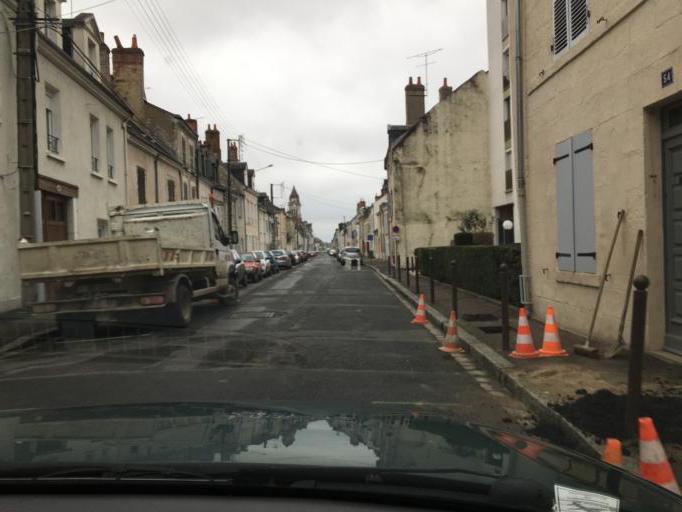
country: FR
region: Centre
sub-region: Departement du Loiret
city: Saint-Jean-le-Blanc
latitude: 47.8928
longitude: 1.9064
